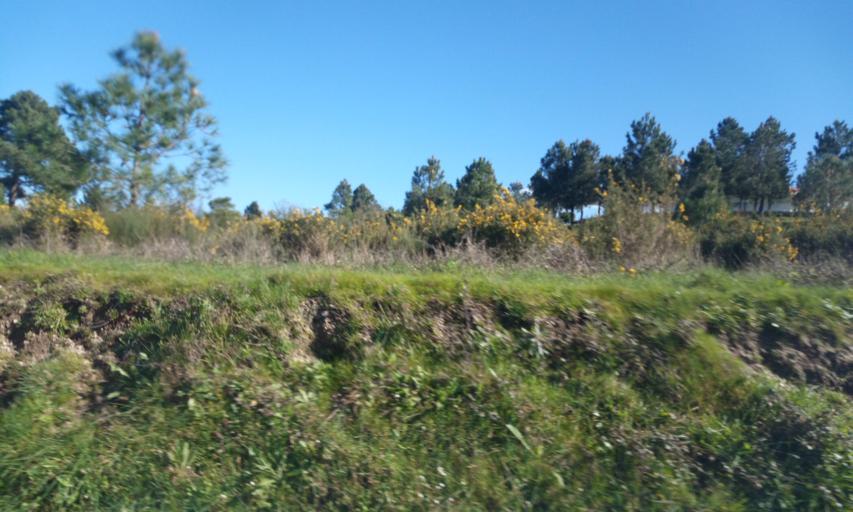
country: PT
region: Guarda
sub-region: Seia
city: Seia
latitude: 40.4727
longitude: -7.6246
